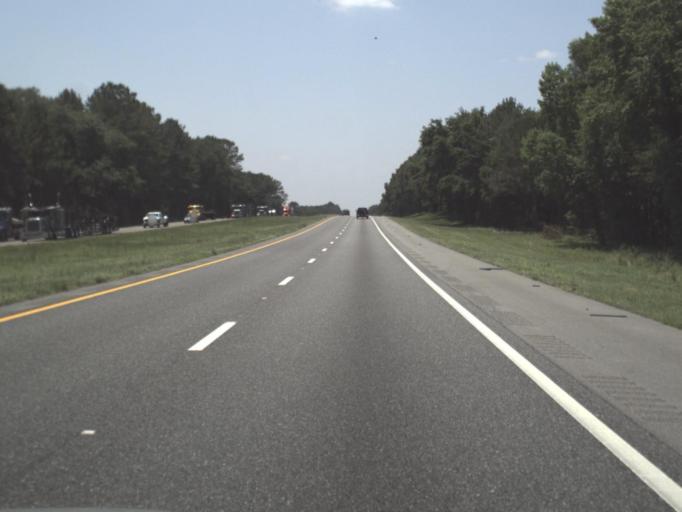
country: US
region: Florida
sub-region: Columbia County
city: Five Points
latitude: 30.2499
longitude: -82.7051
